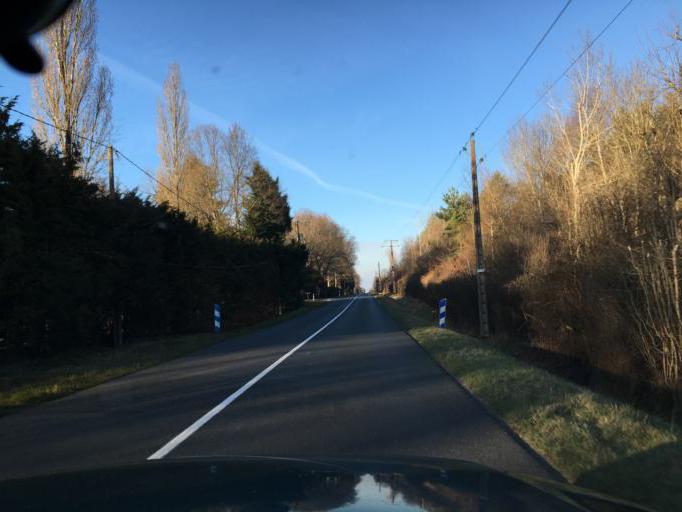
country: FR
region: Centre
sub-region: Departement du Loiret
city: Jouy-le-Potier
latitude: 47.7209
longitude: 1.7990
